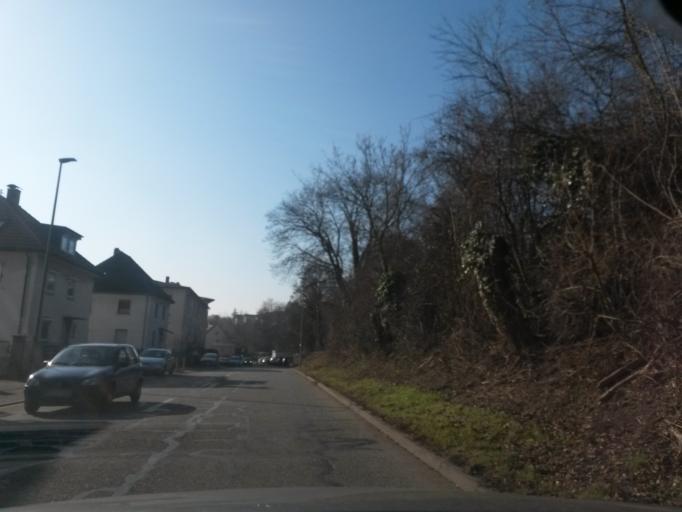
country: DE
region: Baden-Wuerttemberg
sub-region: Karlsruhe Region
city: Eutingen
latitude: 48.9150
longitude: 8.7531
